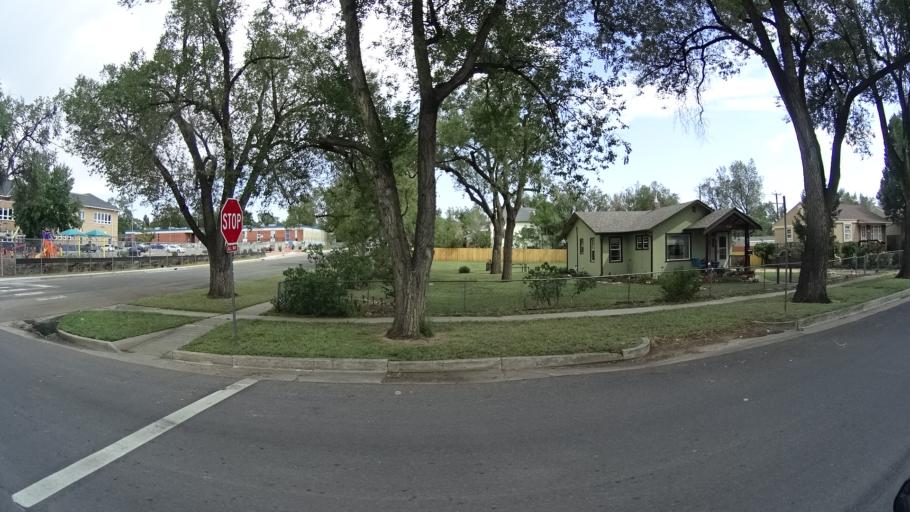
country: US
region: Colorado
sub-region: El Paso County
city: Colorado Springs
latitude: 38.8239
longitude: -104.8083
